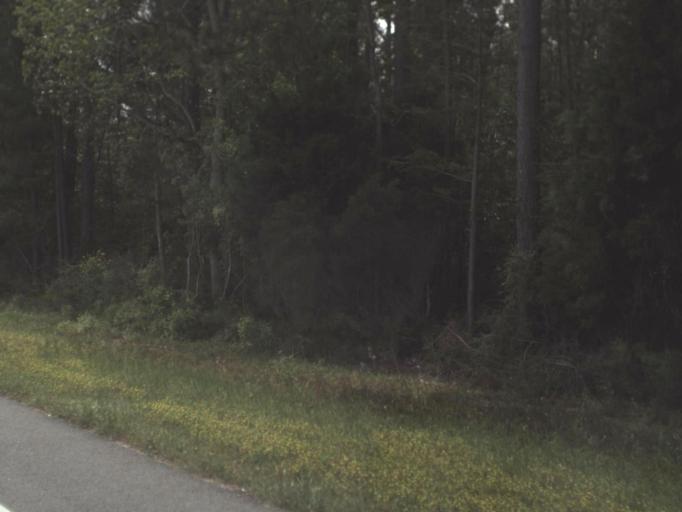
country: US
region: Florida
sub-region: Escambia County
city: Myrtle Grove
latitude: 30.3747
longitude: -87.3555
